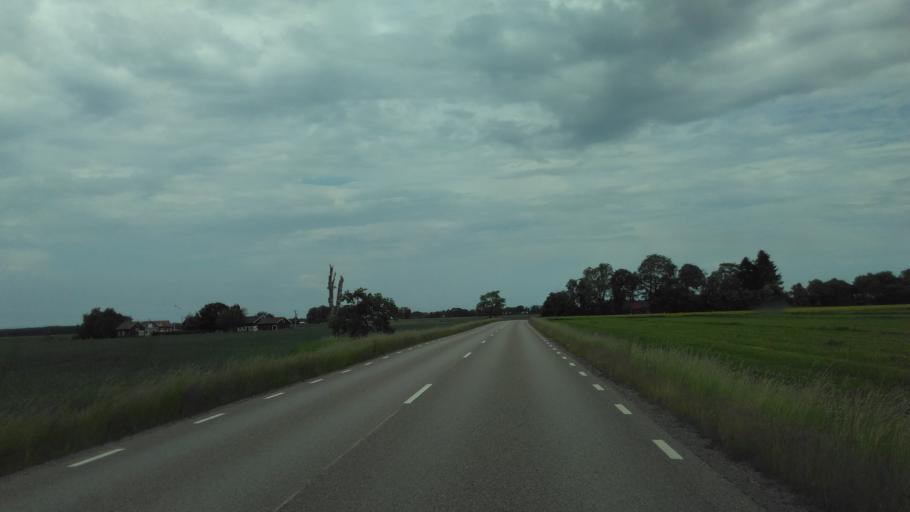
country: SE
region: Vaestra Goetaland
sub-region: Lidkopings Kommun
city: Lidkoping
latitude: 58.4048
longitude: 13.1630
